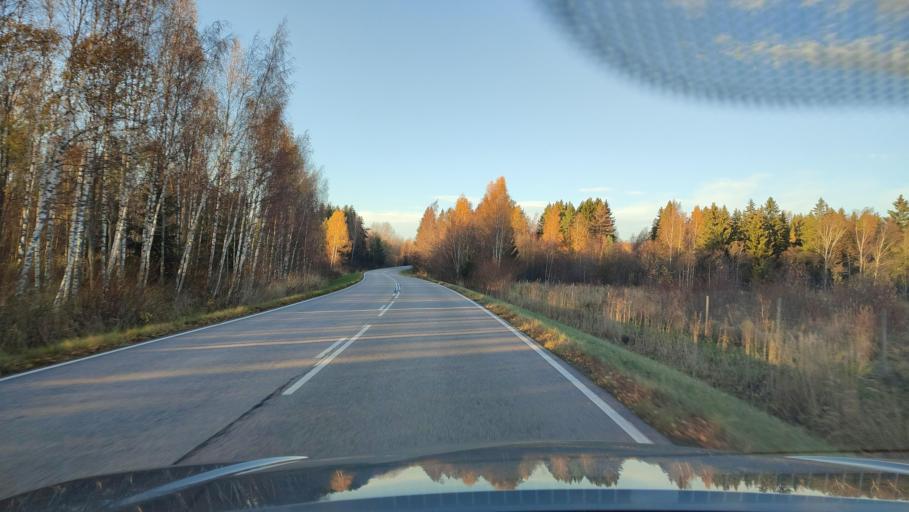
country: FI
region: Ostrobothnia
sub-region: Sydosterbotten
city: Kristinestad
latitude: 62.2849
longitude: 21.3782
